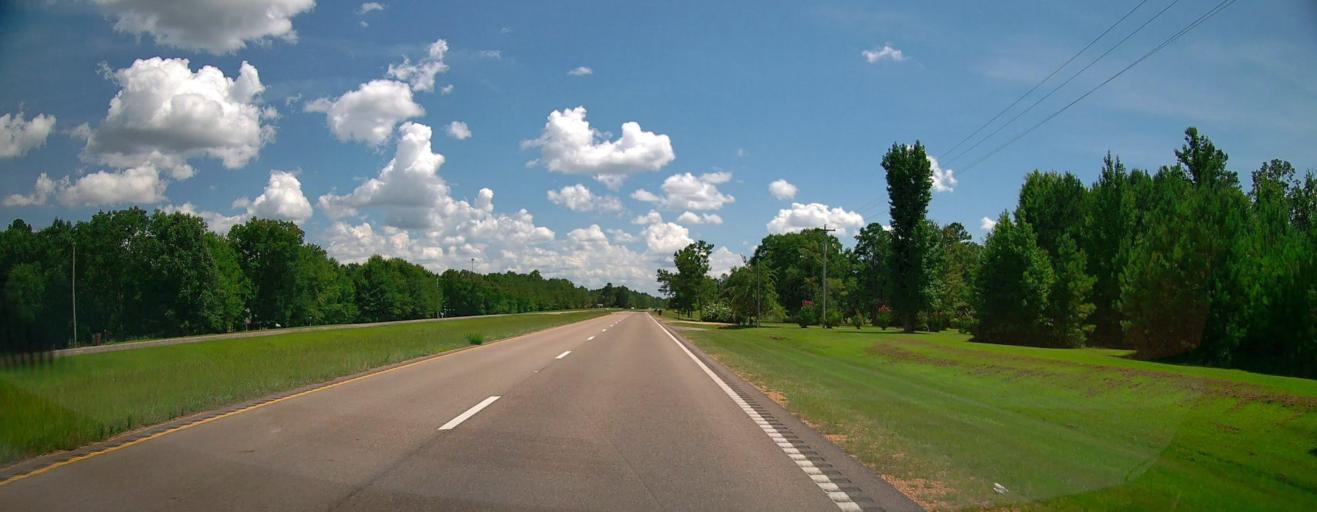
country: US
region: Mississippi
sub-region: Monroe County
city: Aberdeen
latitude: 33.9328
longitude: -88.5969
